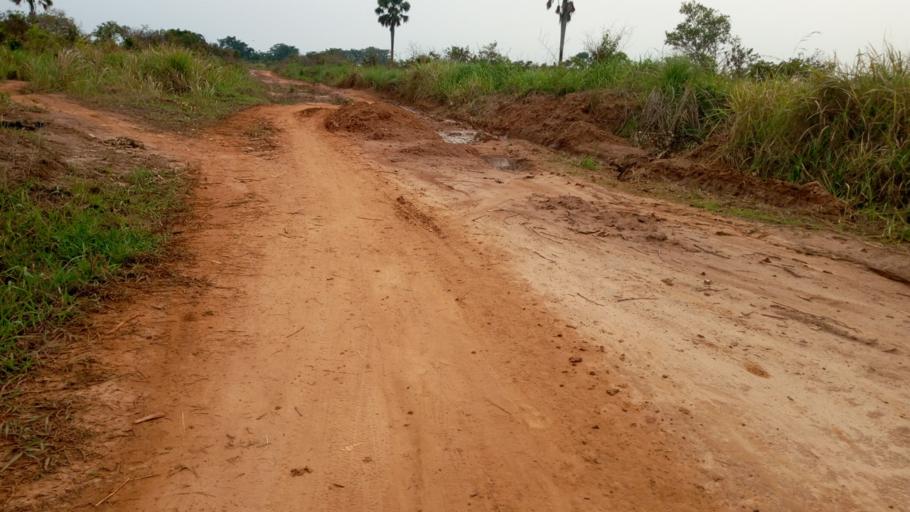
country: CD
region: Bandundu
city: Bandundu
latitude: -3.4675
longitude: 17.7140
